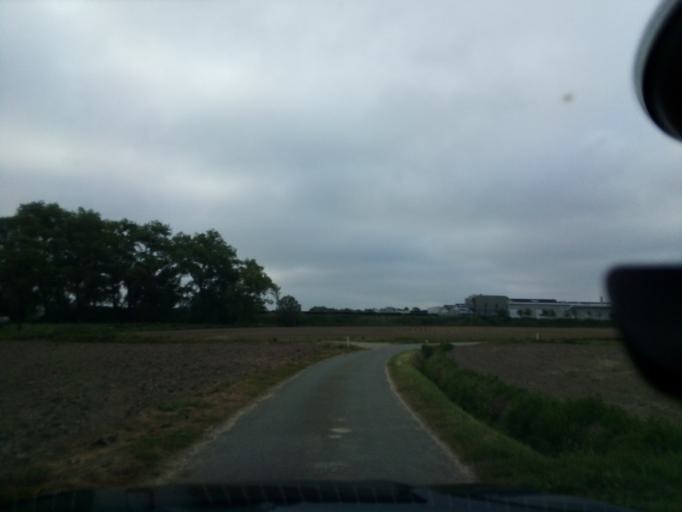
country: BE
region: Flanders
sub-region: Provincie West-Vlaanderen
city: Ingelmunster
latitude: 50.9419
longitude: 3.2643
